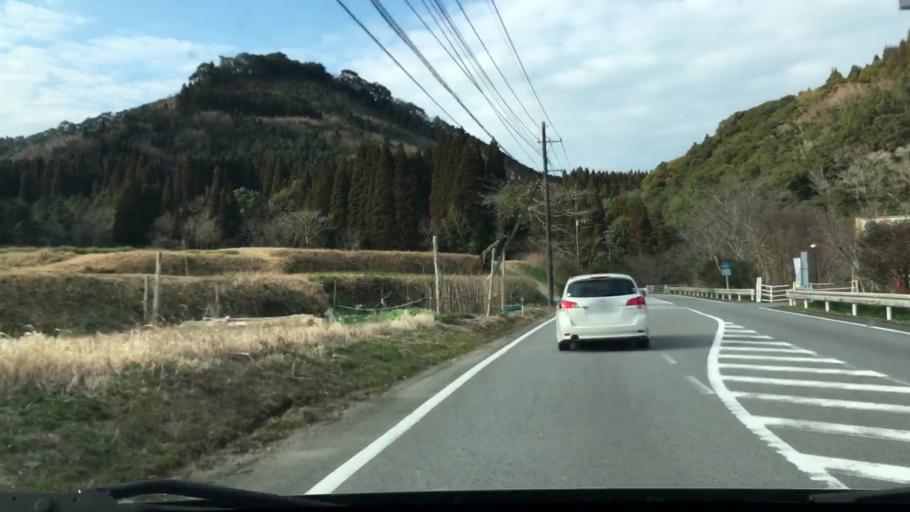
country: JP
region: Miyazaki
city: Nichinan
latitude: 31.7456
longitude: 131.3358
